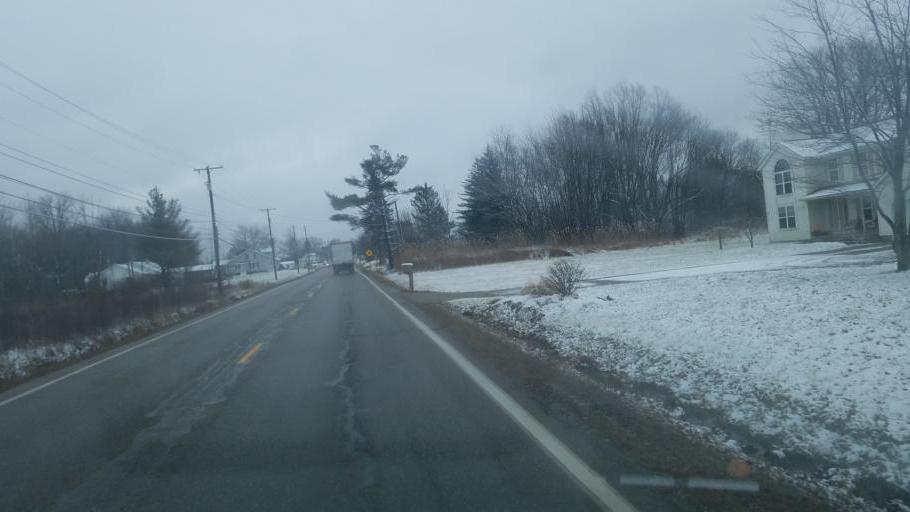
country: US
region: Ohio
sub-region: Portage County
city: Garrettsville
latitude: 41.2358
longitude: -81.1396
